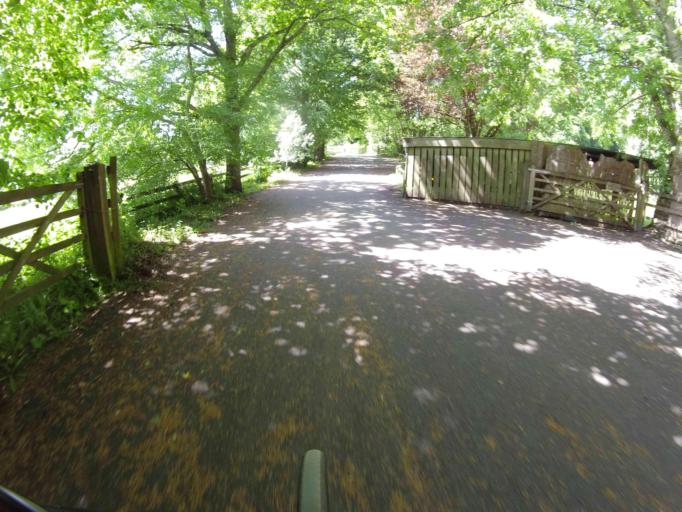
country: GB
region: England
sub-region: Devon
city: Bovey Tracey
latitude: 50.6560
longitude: -3.7507
